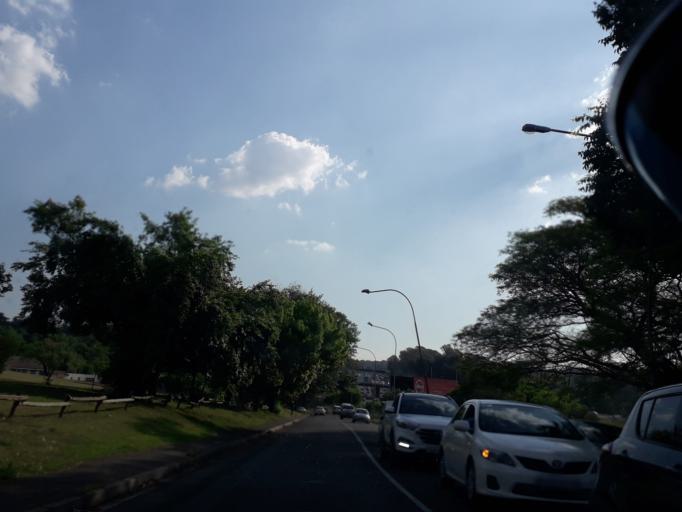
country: ZA
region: Gauteng
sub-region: City of Johannesburg Metropolitan Municipality
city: Johannesburg
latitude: -26.1368
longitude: 28.0705
